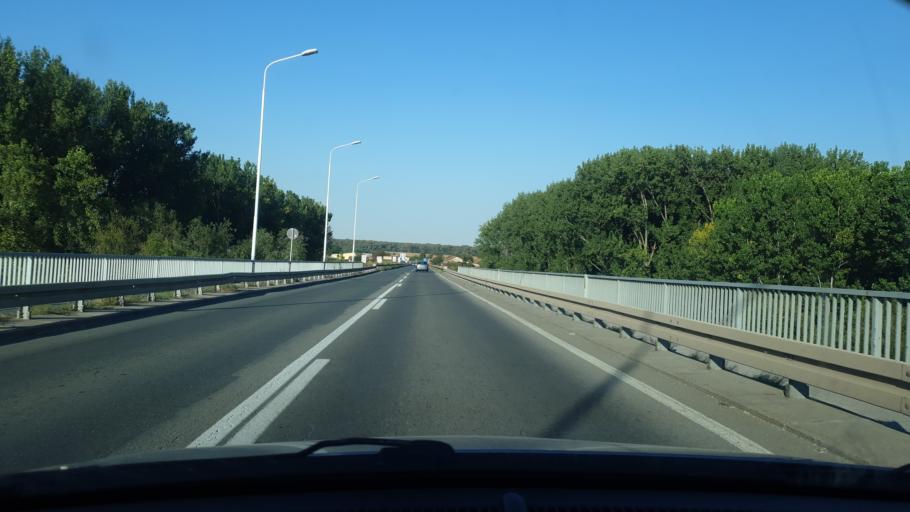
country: RS
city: Klenak
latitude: 44.7604
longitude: 19.7166
